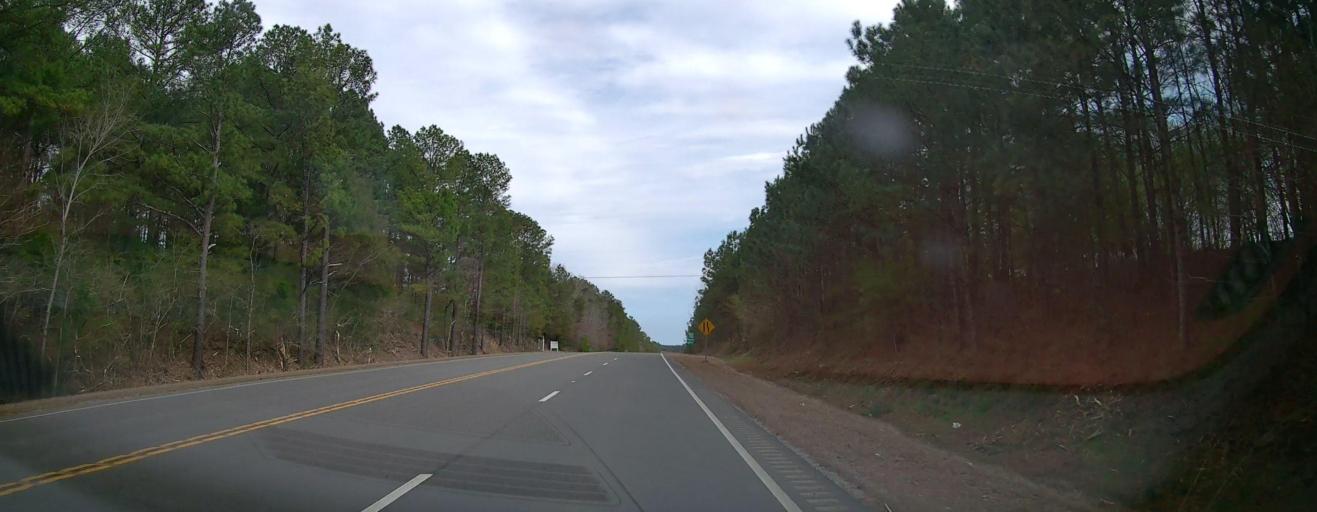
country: US
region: Alabama
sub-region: Walker County
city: Jasper
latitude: 33.8626
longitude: -87.3893
